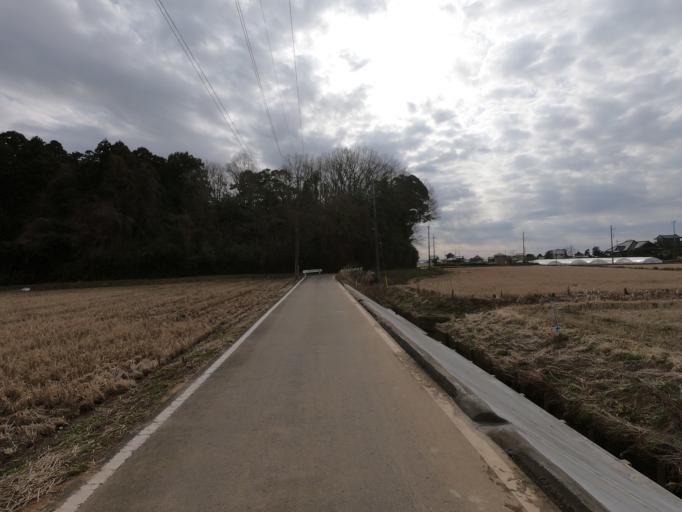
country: JP
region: Ibaraki
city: Inashiki
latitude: 36.0595
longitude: 140.4421
